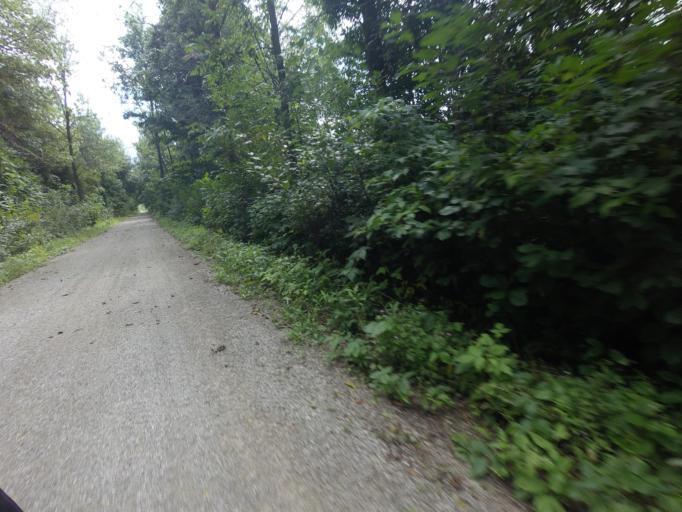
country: CA
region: Ontario
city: Huron East
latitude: 43.6235
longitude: -81.1620
